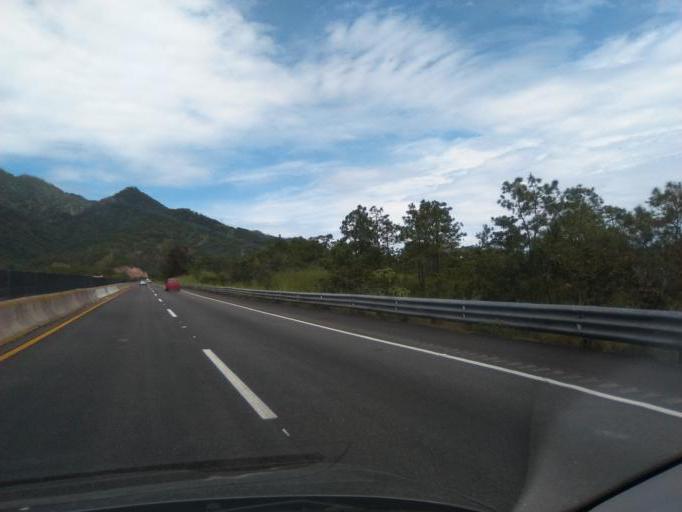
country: MX
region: Guerrero
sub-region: Chilpancingo de los Bravo
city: Cajelitos
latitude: 17.2884
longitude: -99.5051
